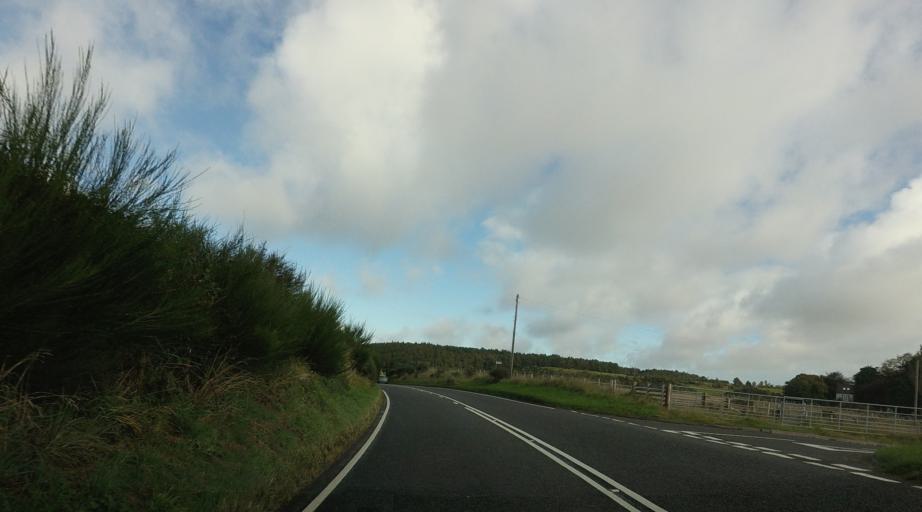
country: GB
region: Scotland
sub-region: Fife
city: Balmullo
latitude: 56.3870
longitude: -2.9134
